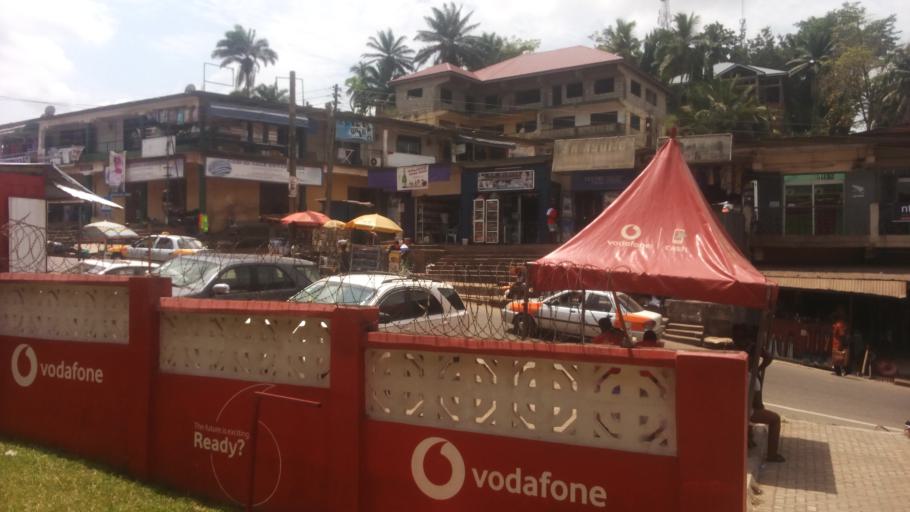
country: GH
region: Western
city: Tarkwa
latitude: 5.3059
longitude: -1.9941
